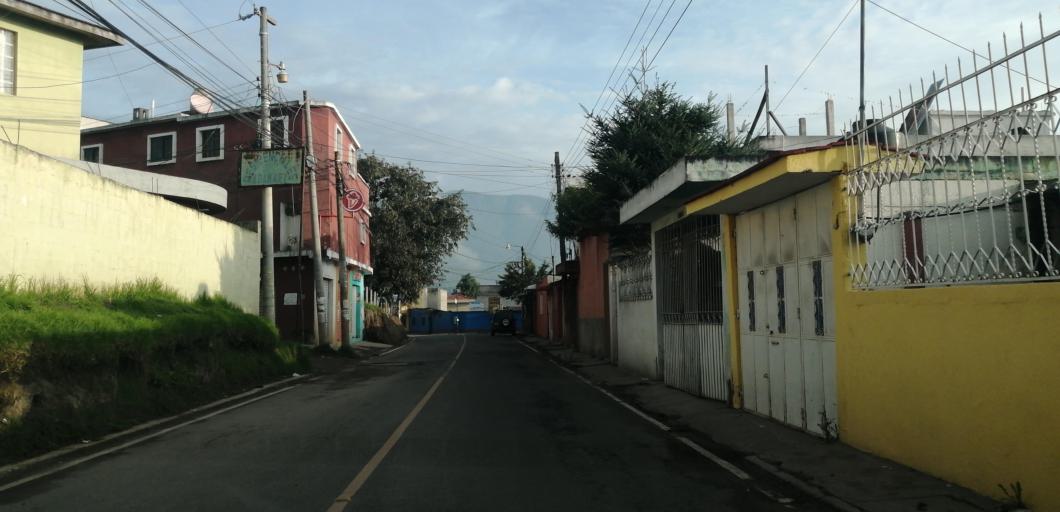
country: GT
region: Quetzaltenango
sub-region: Municipio de La Esperanza
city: La Esperanza
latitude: 14.8662
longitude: -91.5545
